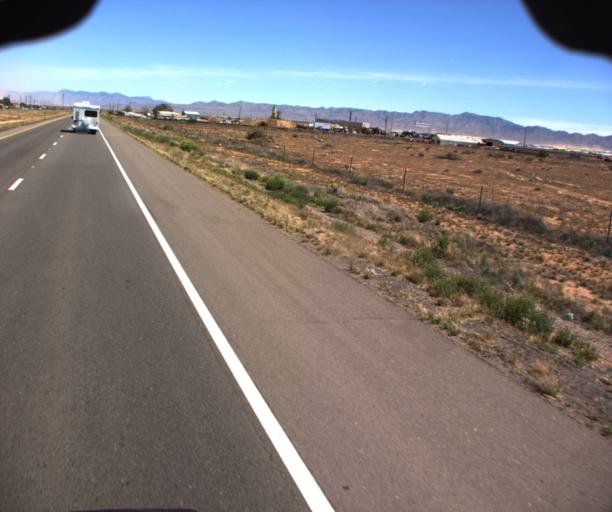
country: US
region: Arizona
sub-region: Mohave County
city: New Kingman-Butler
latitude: 35.2501
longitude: -113.9788
